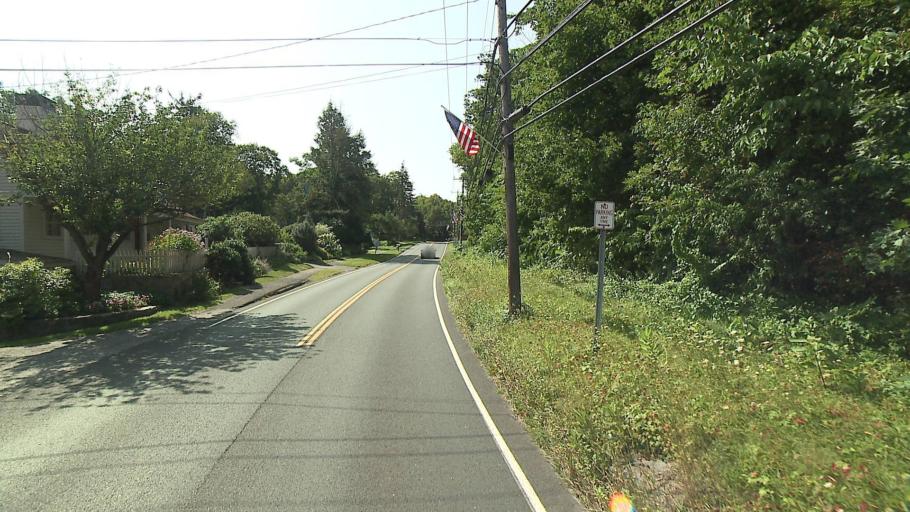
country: US
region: Connecticut
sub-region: Fairfield County
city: Danbury
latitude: 41.4691
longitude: -73.3891
